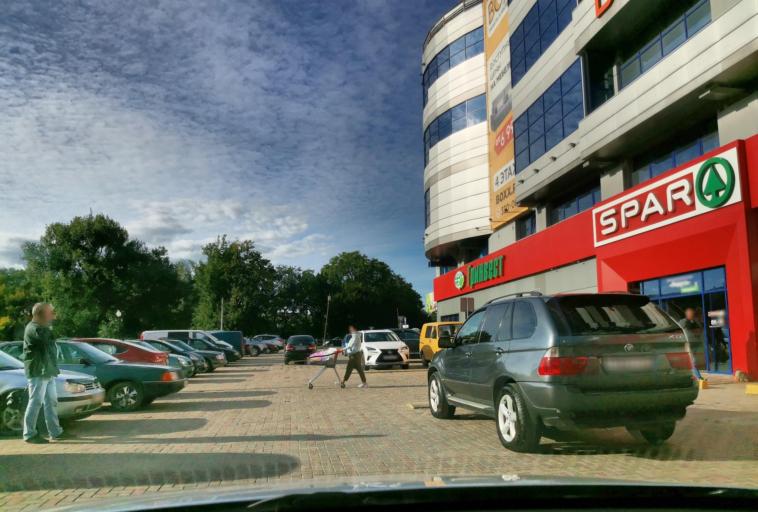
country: RU
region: Kaliningrad
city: Chernyakhovsk
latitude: 54.6355
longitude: 21.8059
